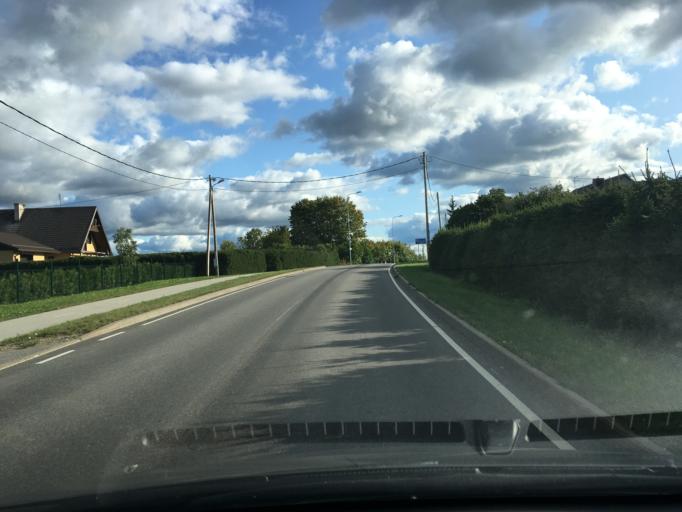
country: EE
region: Harju
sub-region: Joelaehtme vald
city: Loo
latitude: 59.4129
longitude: 24.9473
